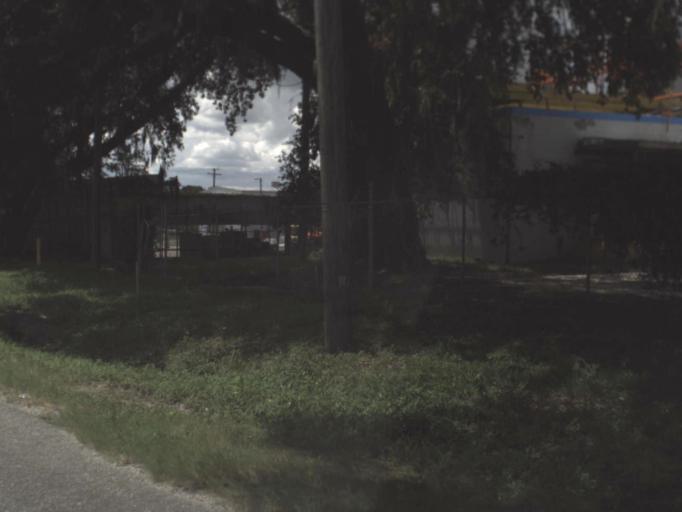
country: US
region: Florida
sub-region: Hillsborough County
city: Dover
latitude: 27.9908
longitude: -82.2365
